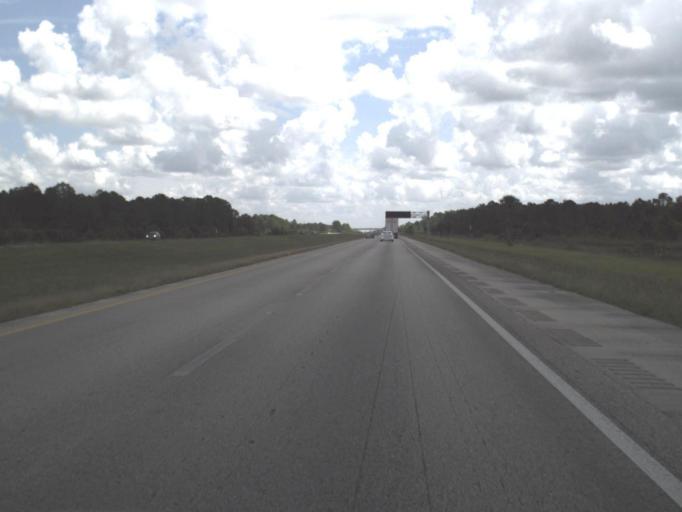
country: US
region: Florida
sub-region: Collier County
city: Golden Gate
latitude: 26.1530
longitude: -81.5621
